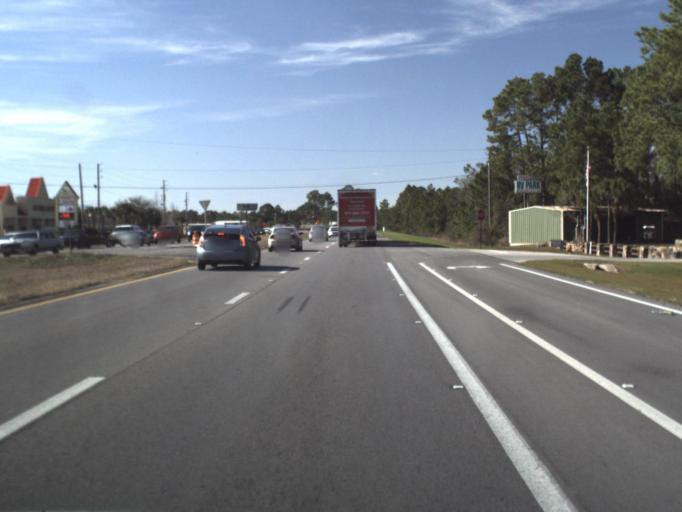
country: US
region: Florida
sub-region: Bay County
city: Panama City Beach
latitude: 30.2032
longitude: -85.8232
